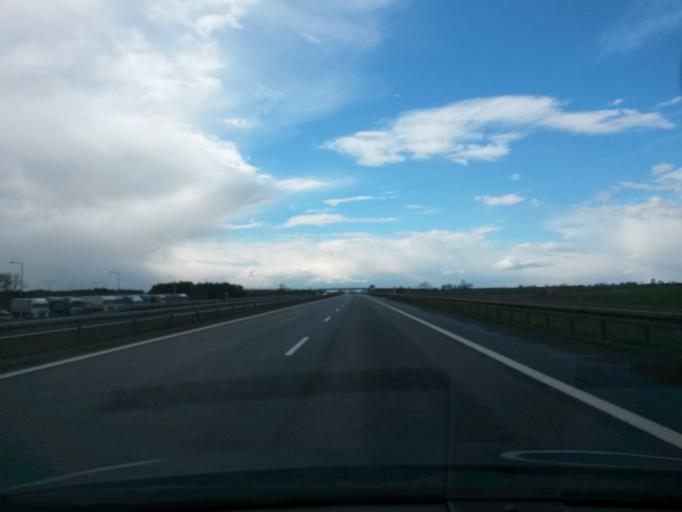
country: PL
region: Greater Poland Voivodeship
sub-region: Powiat slupecki
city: Ladek
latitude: 52.2264
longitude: 17.9330
